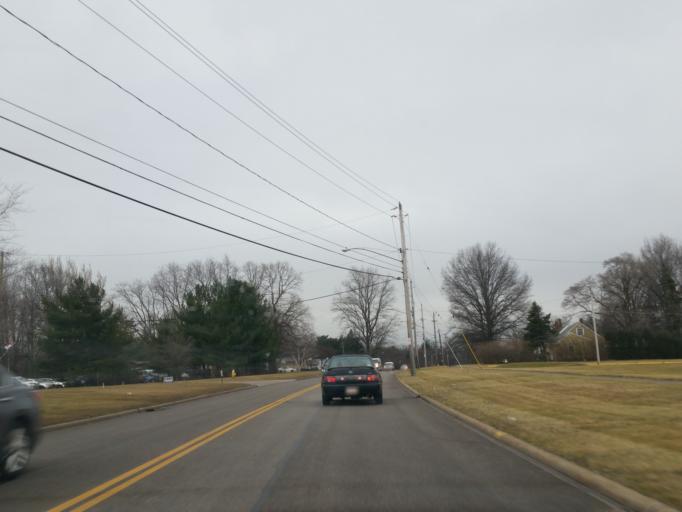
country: US
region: Ohio
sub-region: Cuyahoga County
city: Parma Heights
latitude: 41.4162
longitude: -81.7569
